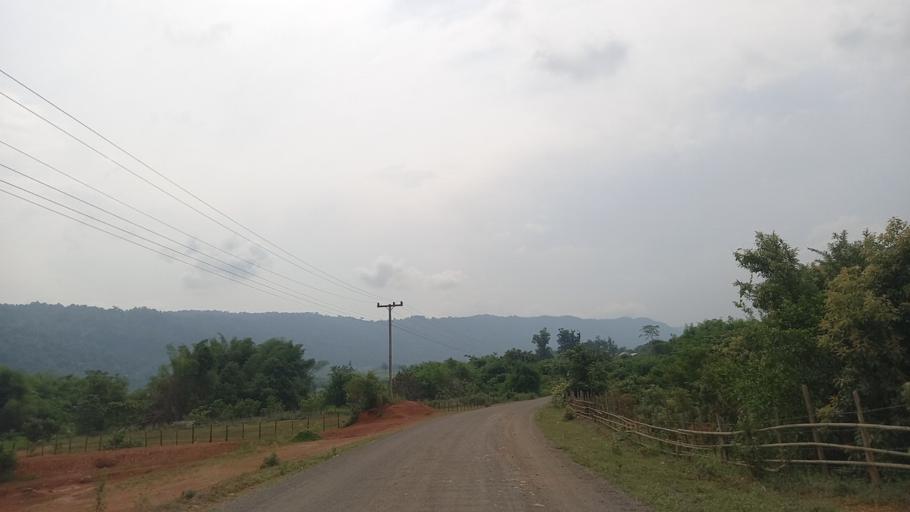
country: LA
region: Bolikhamxai
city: Ban Nahin
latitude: 18.1440
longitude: 104.7535
